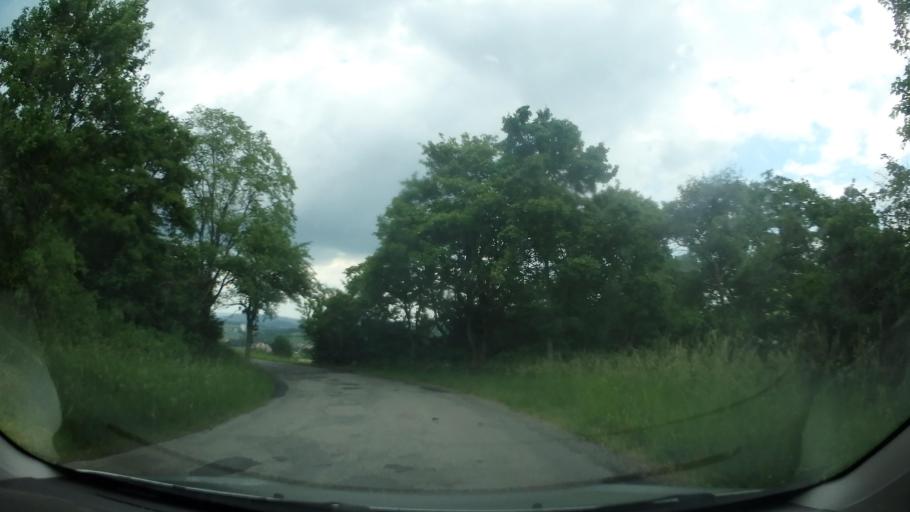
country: CZ
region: South Moravian
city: Doubravice nad Svitavou
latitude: 49.4594
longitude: 16.6028
